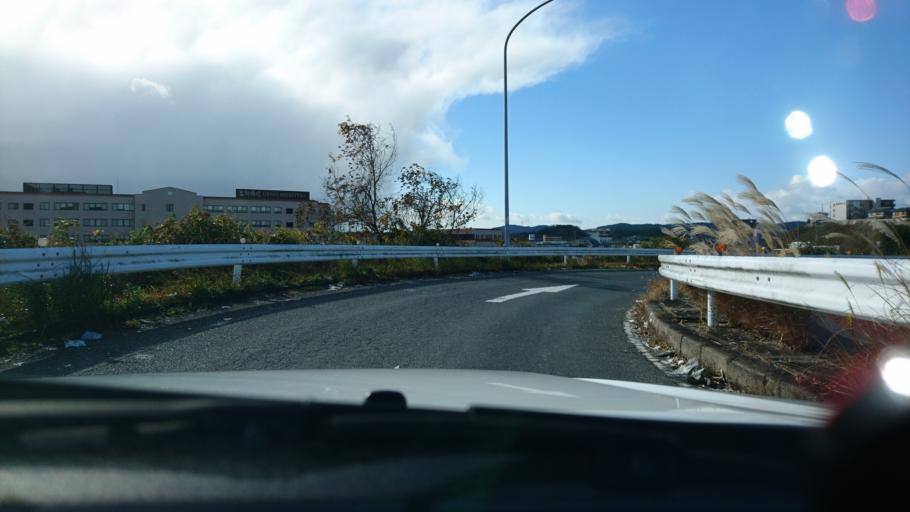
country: JP
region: Mie
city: Ueno-ebisumachi
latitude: 34.7531
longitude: 136.1481
